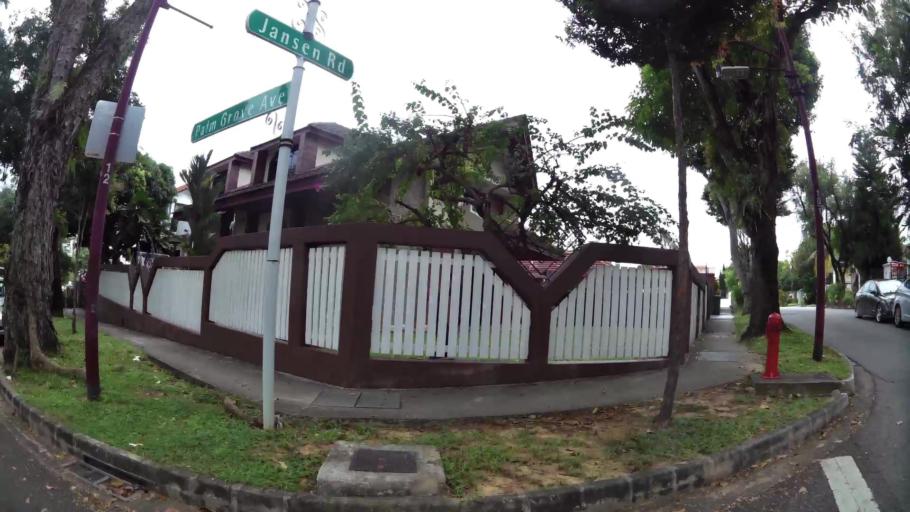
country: SG
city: Singapore
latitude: 1.3594
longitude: 103.8775
